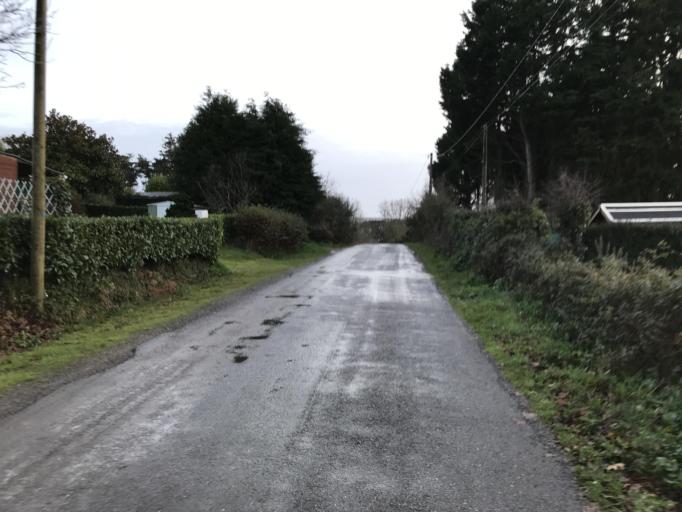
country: FR
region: Brittany
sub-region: Departement du Finistere
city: Logonna-Daoulas
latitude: 48.3196
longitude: -4.3128
